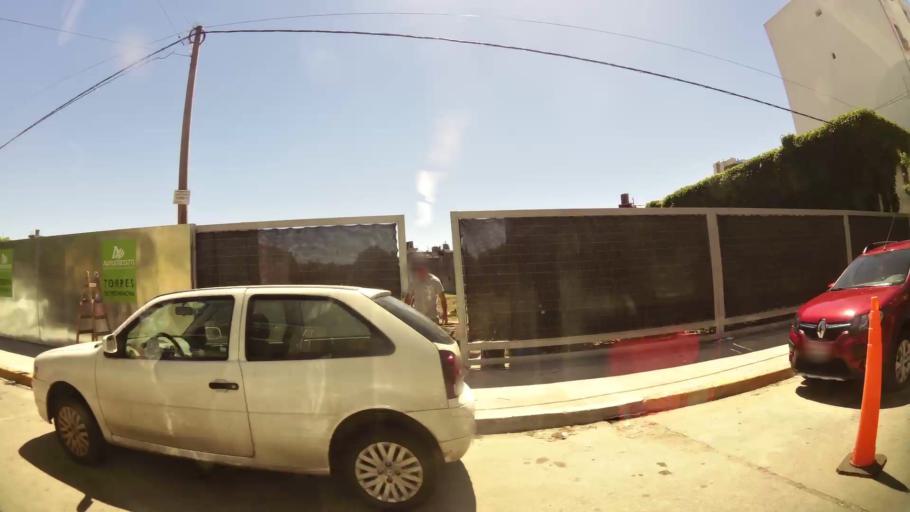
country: AR
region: Santa Fe
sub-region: Departamento de Rosario
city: Rosario
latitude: -32.9332
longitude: -60.6535
